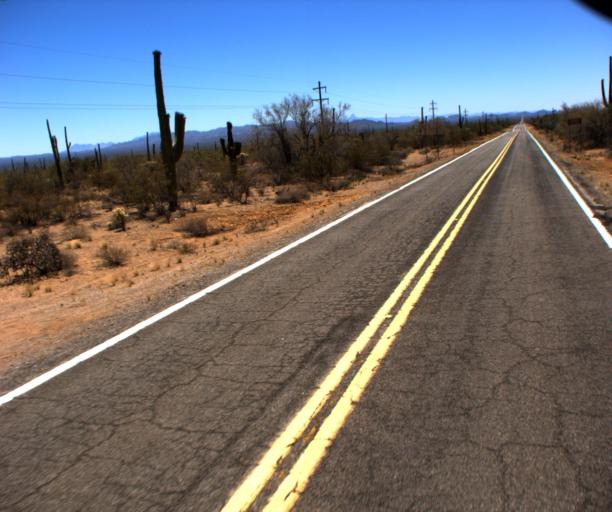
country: US
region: Arizona
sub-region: Pima County
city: Sells
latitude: 32.1383
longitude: -112.0963
